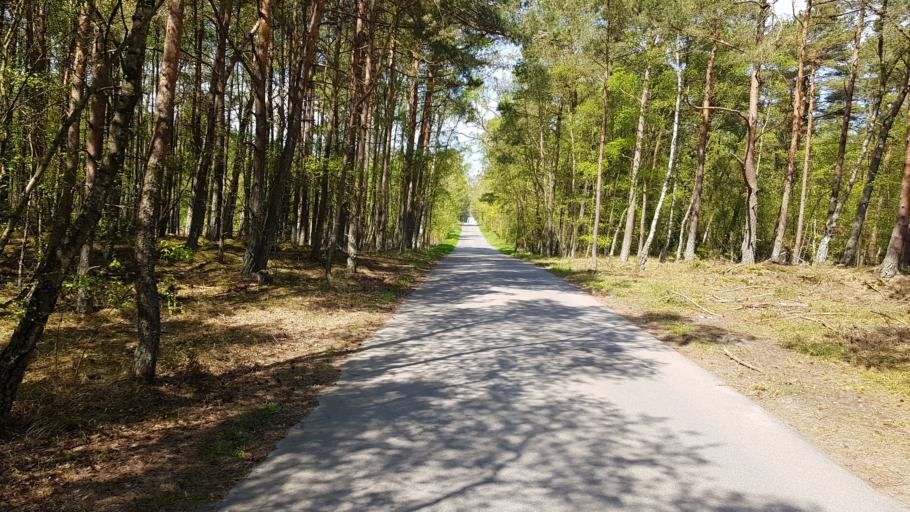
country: DK
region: Capital Region
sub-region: Bornholm Kommune
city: Nexo
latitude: 54.9987
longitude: 15.0848
